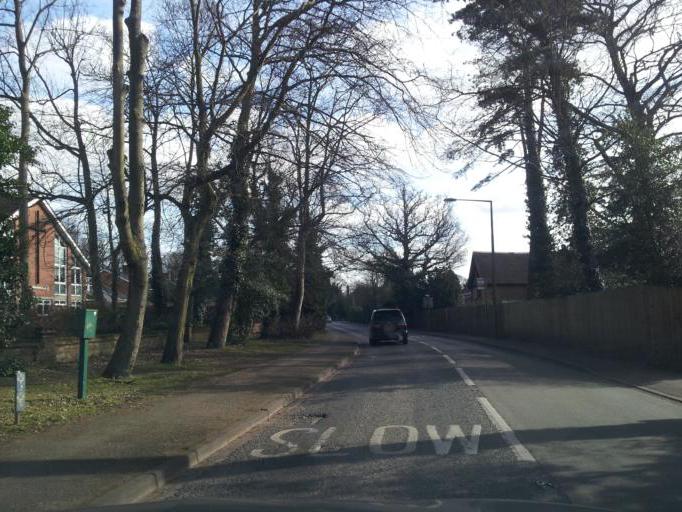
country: GB
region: England
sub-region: Hertfordshire
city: St Albans
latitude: 51.7594
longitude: -0.3121
